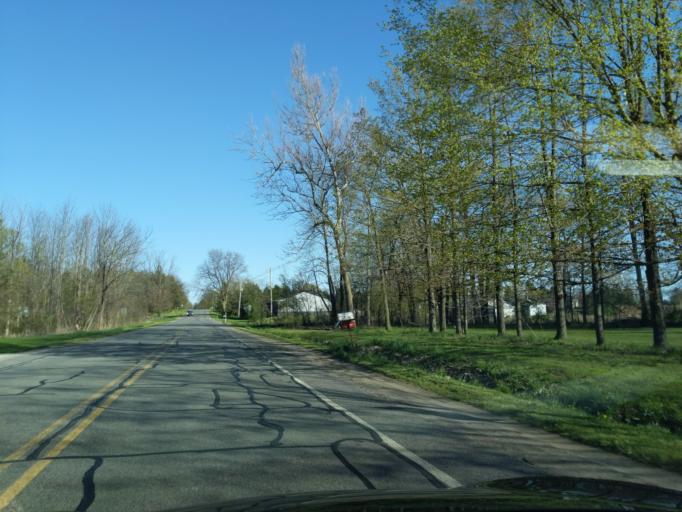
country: US
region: Michigan
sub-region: Ionia County
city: Portland
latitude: 42.8239
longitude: -84.8409
